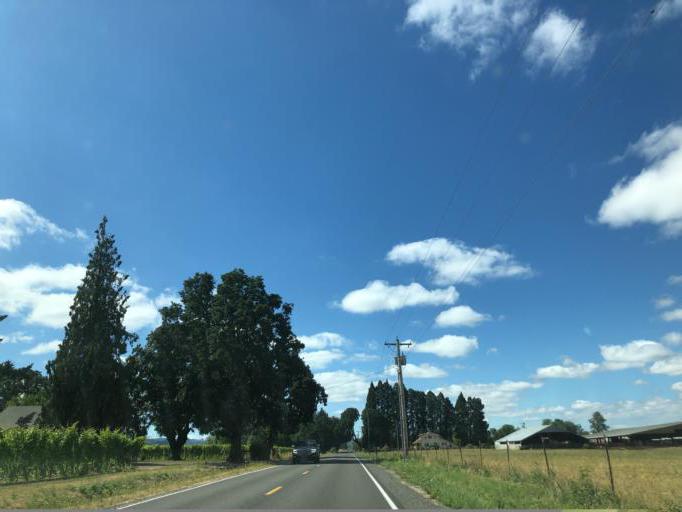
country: US
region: Oregon
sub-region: Marion County
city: Mount Angel
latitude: 45.0767
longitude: -122.7435
